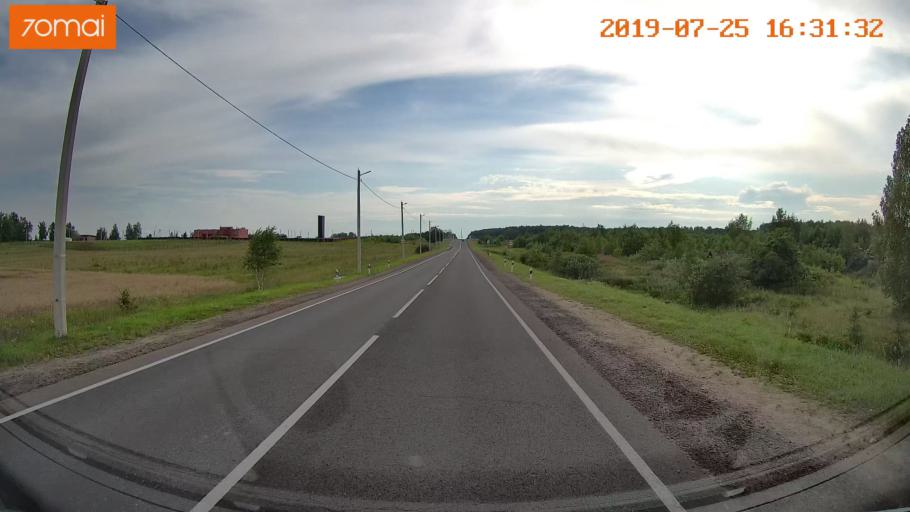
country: RU
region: Ivanovo
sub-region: Privolzhskiy Rayon
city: Ples
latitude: 57.4415
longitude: 41.4833
